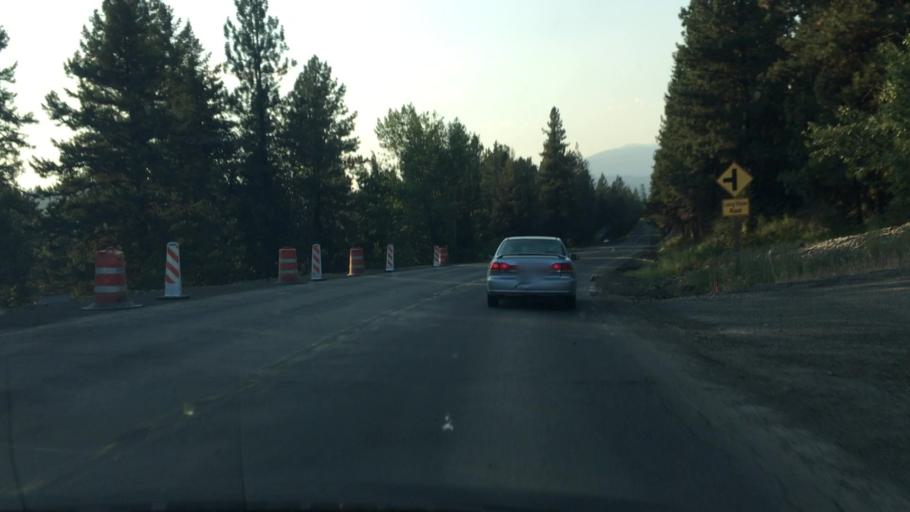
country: US
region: Idaho
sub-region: Valley County
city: McCall
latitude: 44.9319
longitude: -116.1647
